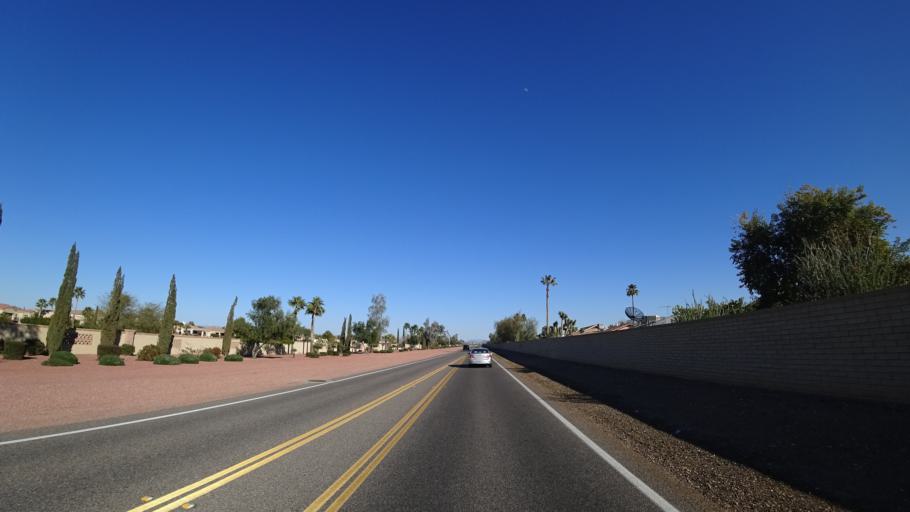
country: US
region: Arizona
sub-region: Maricopa County
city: Sun City West
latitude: 33.6820
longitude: -112.3403
